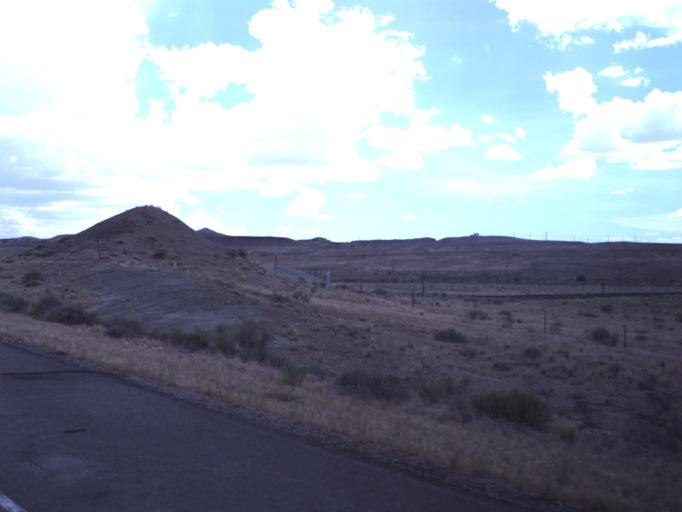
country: US
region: Utah
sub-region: Carbon County
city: East Carbon City
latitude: 38.9852
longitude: -110.1254
